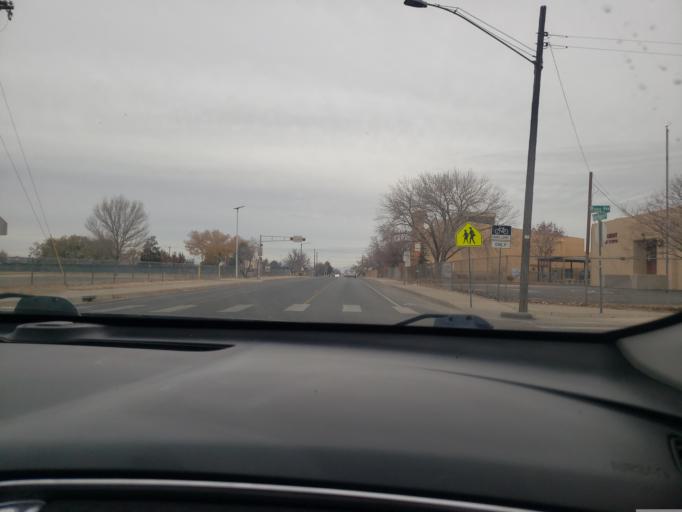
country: US
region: New Mexico
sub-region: Bernalillo County
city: Albuquerque
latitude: 35.0618
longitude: -106.5775
